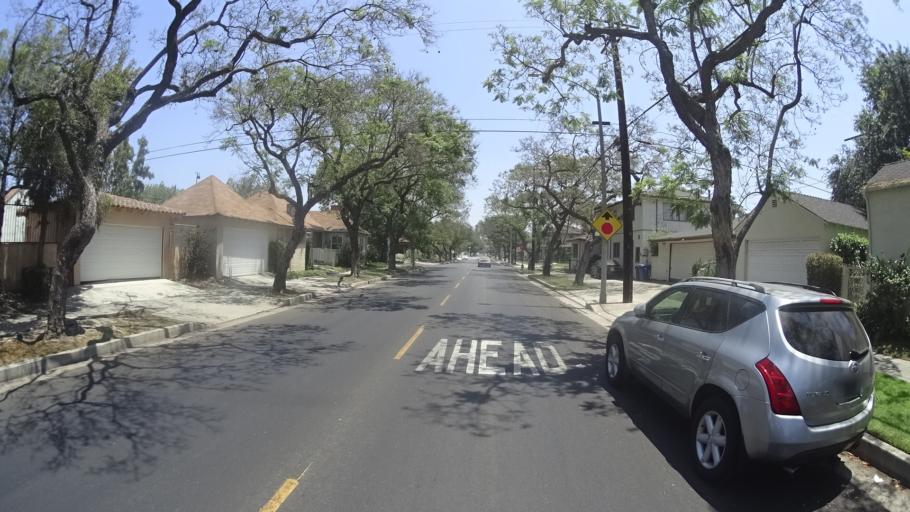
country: US
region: California
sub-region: Los Angeles County
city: View Park-Windsor Hills
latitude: 34.0146
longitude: -118.3249
